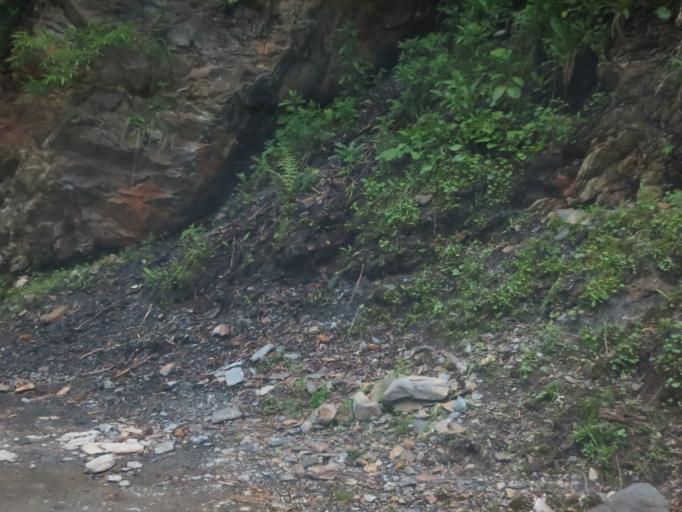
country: GE
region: Kakheti
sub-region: Telavi
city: Telavi
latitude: 42.2335
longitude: 45.4883
